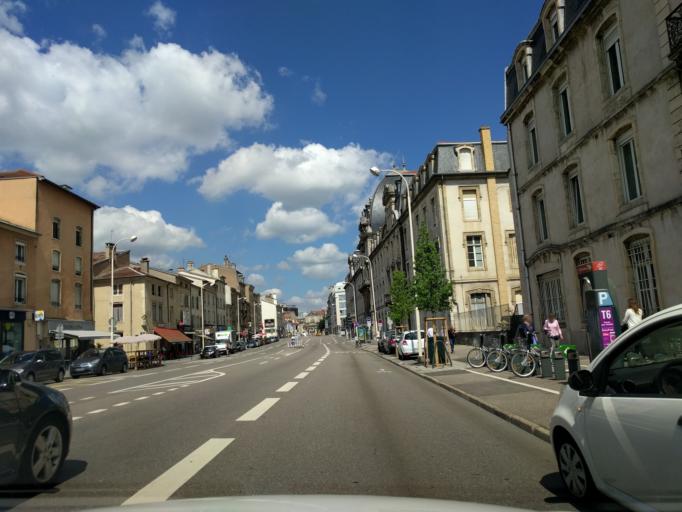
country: FR
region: Lorraine
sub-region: Departement de Meurthe-et-Moselle
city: Nancy
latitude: 48.6833
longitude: 6.1903
